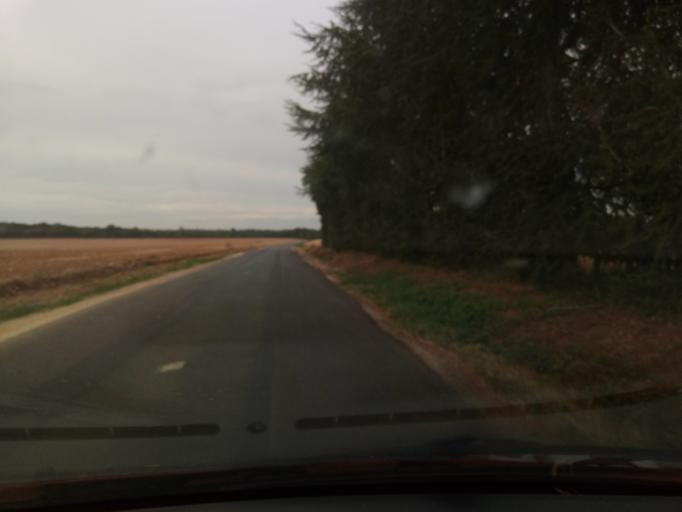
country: FR
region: Poitou-Charentes
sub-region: Departement de la Vienne
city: Saint-Savin
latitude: 46.5356
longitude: 0.7809
